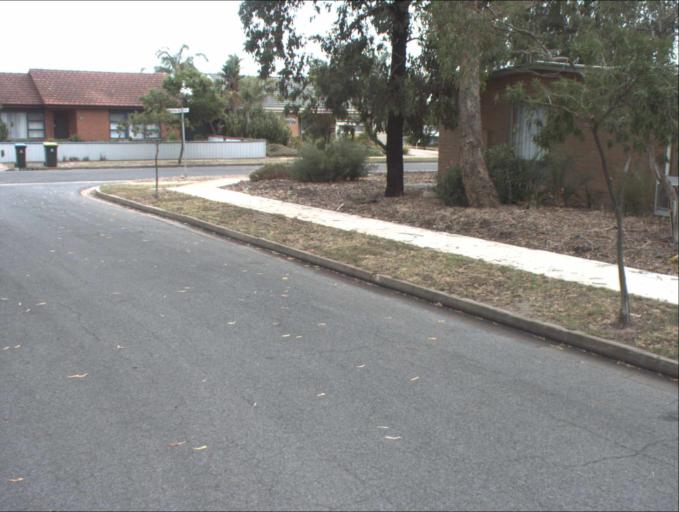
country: AU
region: South Australia
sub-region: Port Adelaide Enfield
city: Birkenhead
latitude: -34.8154
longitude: 138.5056
